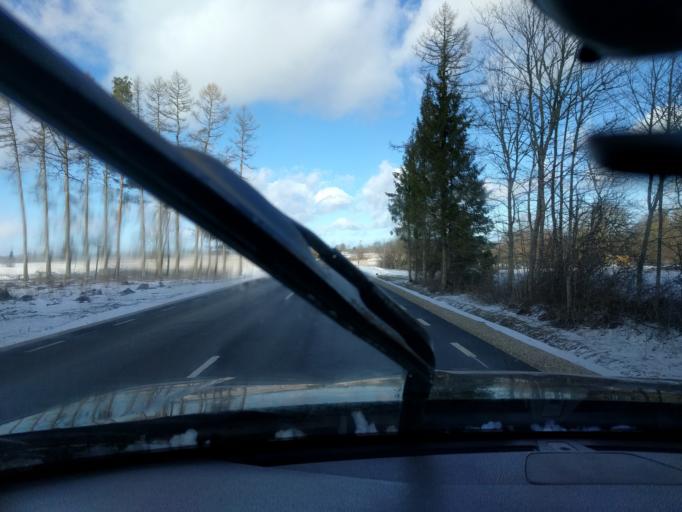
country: EE
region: Harju
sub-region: Raasiku vald
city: Raasiku
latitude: 59.2929
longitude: 25.1811
